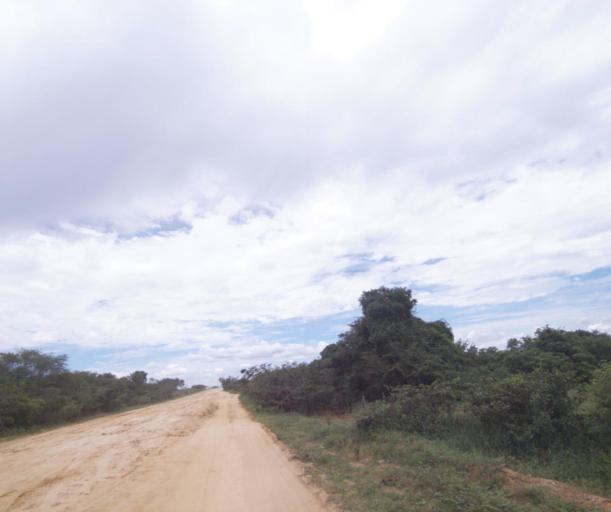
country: BR
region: Bahia
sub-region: Carinhanha
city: Carinhanha
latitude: -14.2769
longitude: -43.7987
